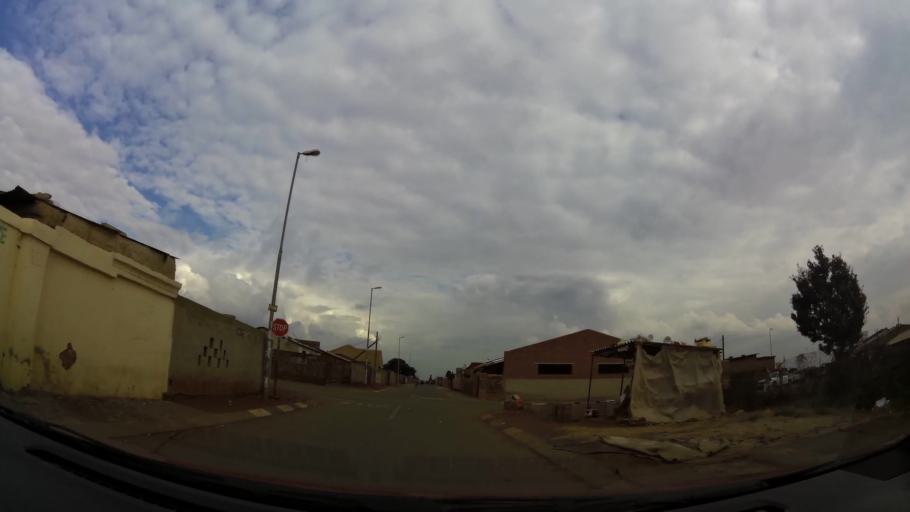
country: ZA
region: Gauteng
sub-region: City of Johannesburg Metropolitan Municipality
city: Soweto
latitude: -26.2454
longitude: 27.8452
